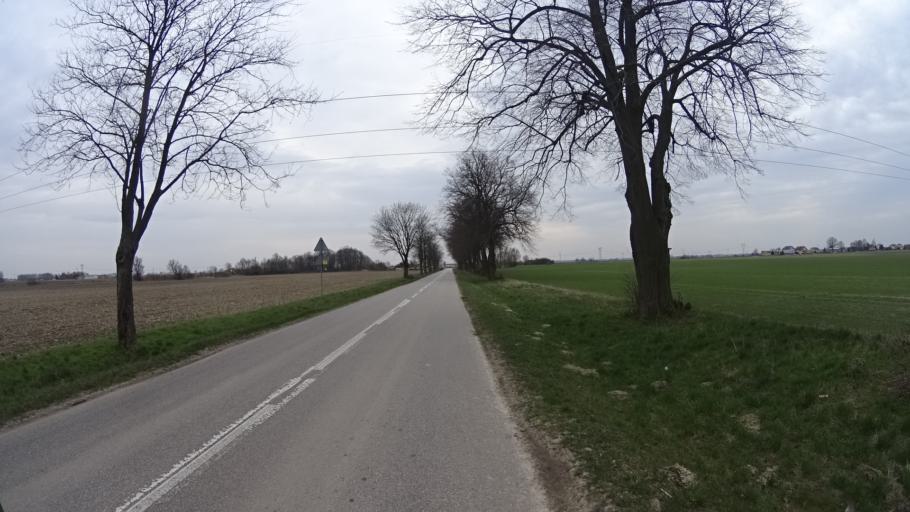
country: PL
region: Masovian Voivodeship
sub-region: Powiat warszawski zachodni
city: Blonie
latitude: 52.2463
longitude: 20.6480
